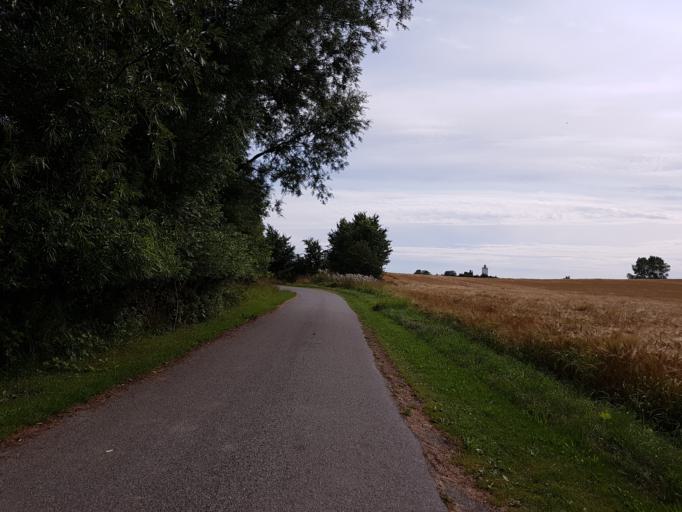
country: DK
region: Zealand
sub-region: Guldborgsund Kommune
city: Nykobing Falster
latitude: 54.5692
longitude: 11.9676
